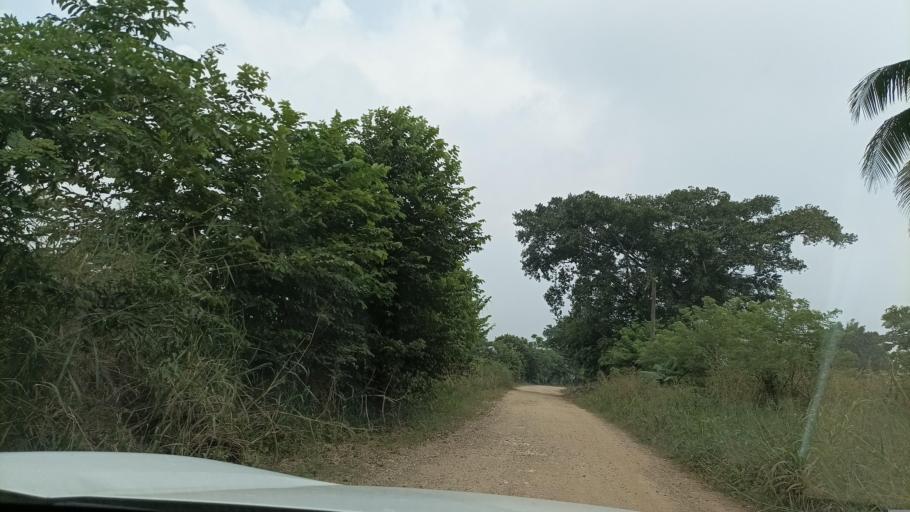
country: MX
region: Veracruz
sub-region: Moloacan
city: Cuichapa
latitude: 17.5802
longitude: -94.2224
